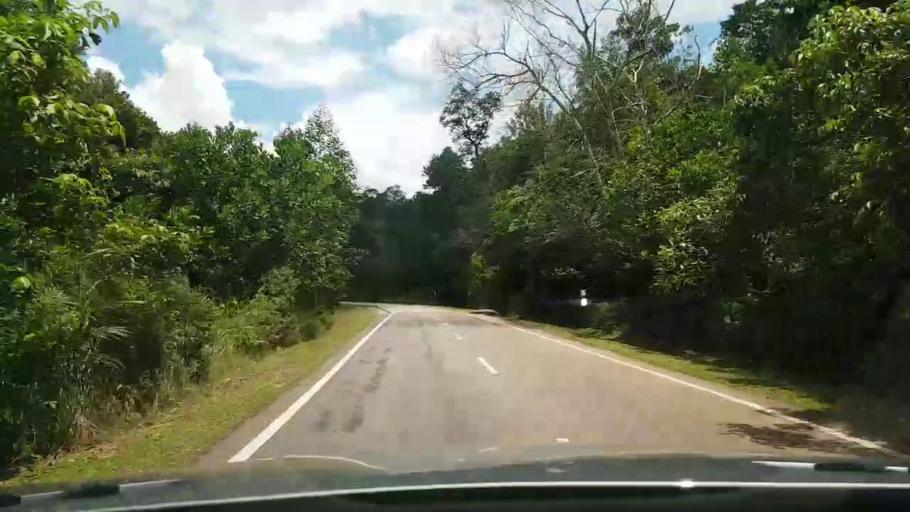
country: MY
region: Pahang
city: Pekan
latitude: 3.1466
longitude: 102.9702
